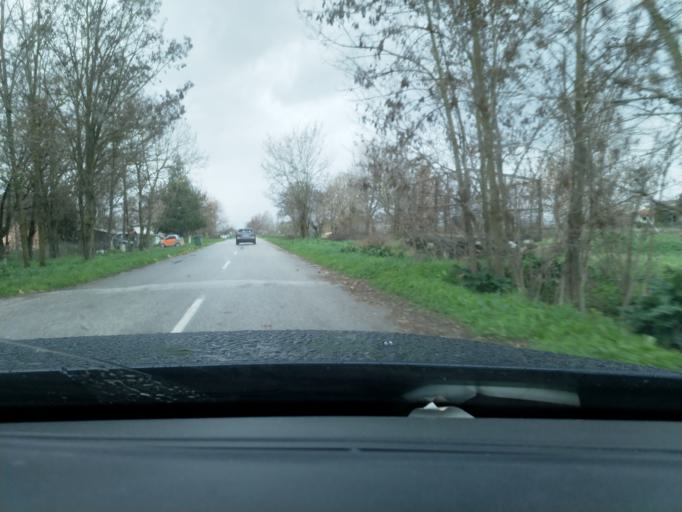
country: GR
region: Thessaly
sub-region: Trikala
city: Taxiarches
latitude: 39.5505
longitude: 21.8948
